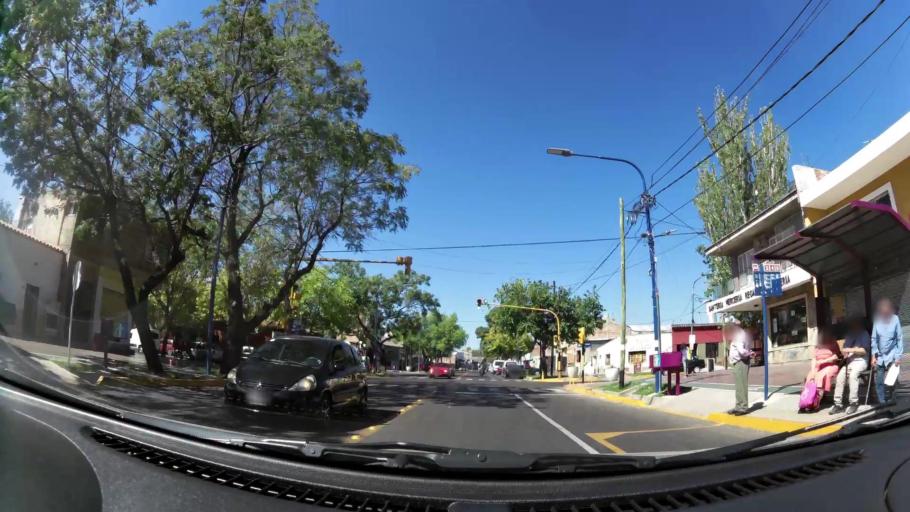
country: AR
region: Mendoza
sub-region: Departamento de Godoy Cruz
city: Godoy Cruz
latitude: -32.9043
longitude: -68.8603
